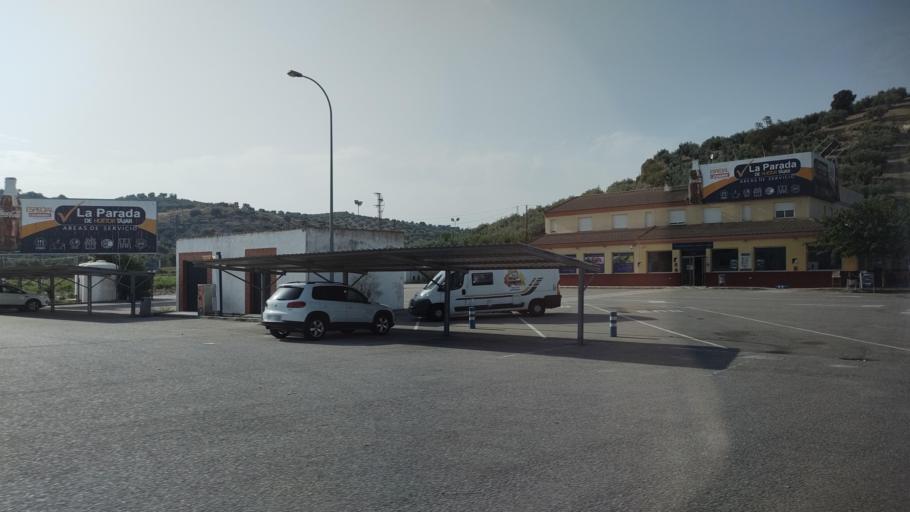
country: ES
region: Andalusia
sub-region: Provincia de Granada
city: Huetor-Tajar
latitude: 37.1797
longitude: -4.0597
